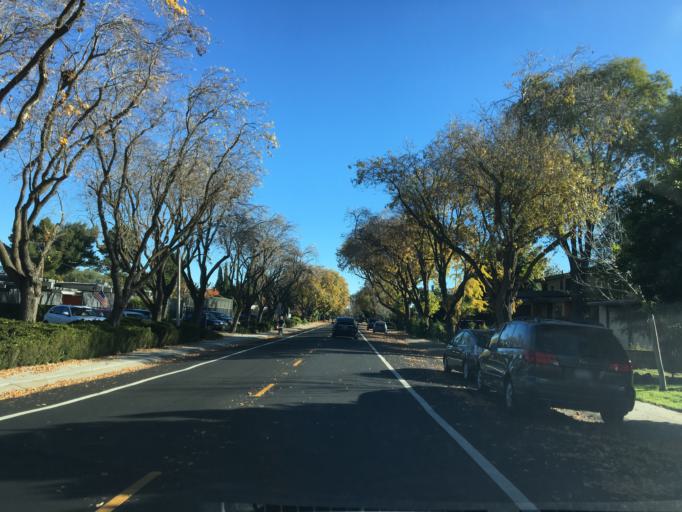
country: US
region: California
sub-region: Santa Clara County
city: Palo Alto
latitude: 37.4304
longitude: -122.1121
